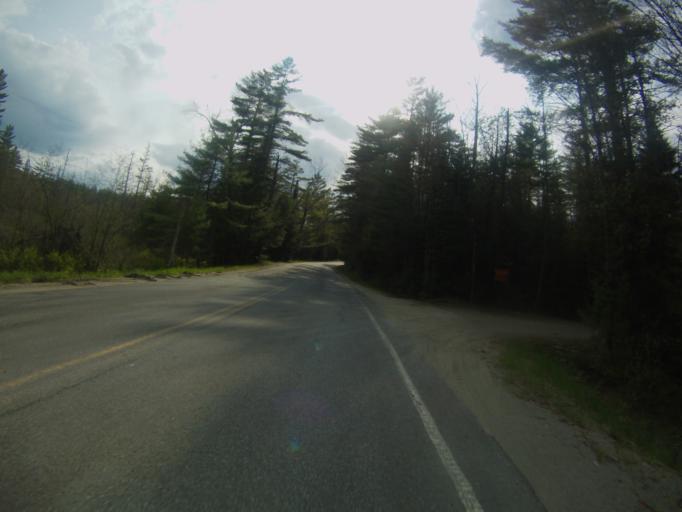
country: US
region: New York
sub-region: Warren County
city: Warrensburg
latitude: 43.8455
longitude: -73.8038
